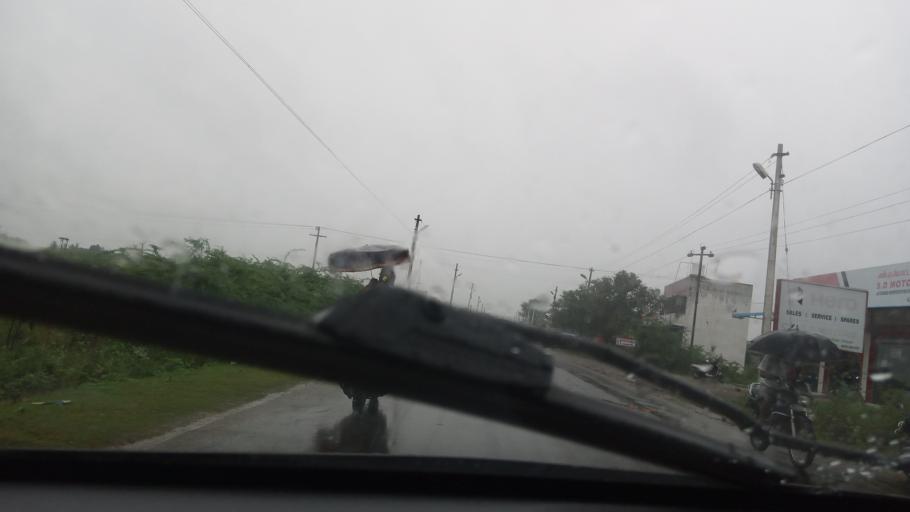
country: IN
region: Tamil Nadu
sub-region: Tiruvannamalai
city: Cheyyar
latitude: 12.6574
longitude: 79.5374
